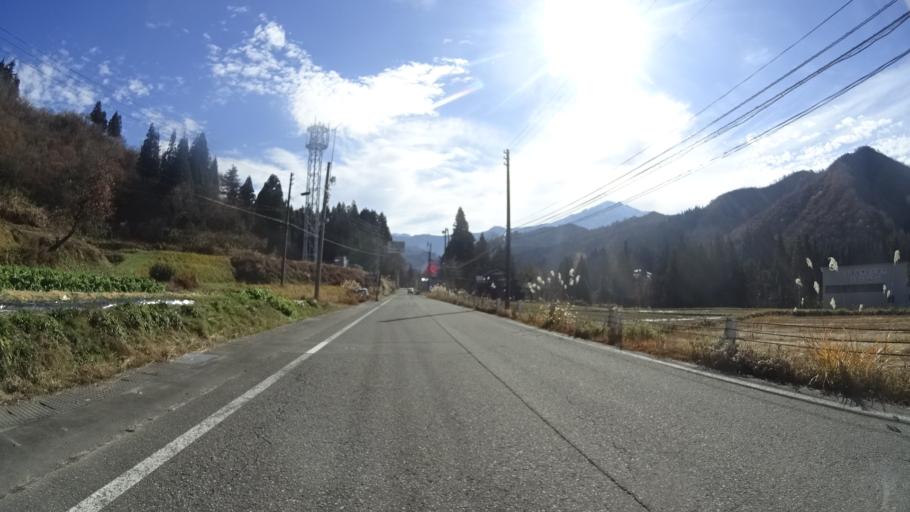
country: JP
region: Niigata
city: Muikamachi
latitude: 37.2016
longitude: 139.0753
